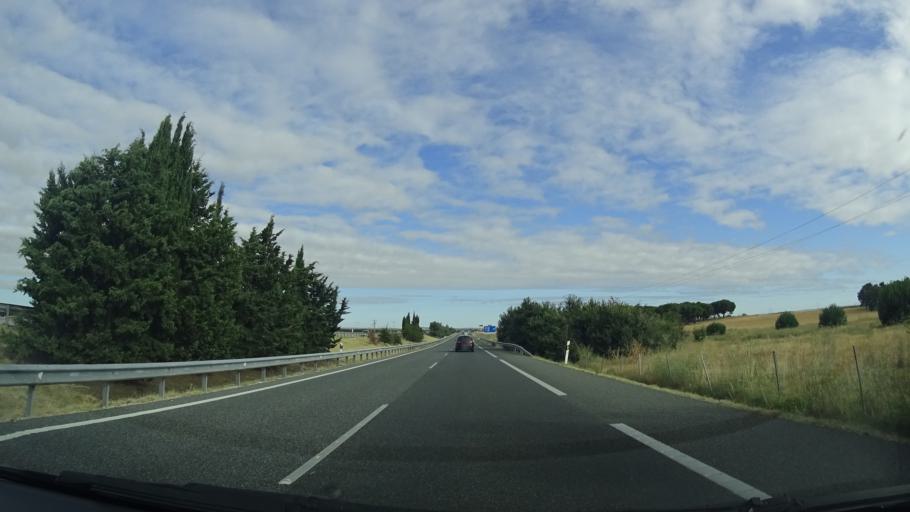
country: ES
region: Castille and Leon
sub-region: Provincia de Valladolid
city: San Vicente del Palacio
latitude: 41.2611
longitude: -4.8781
